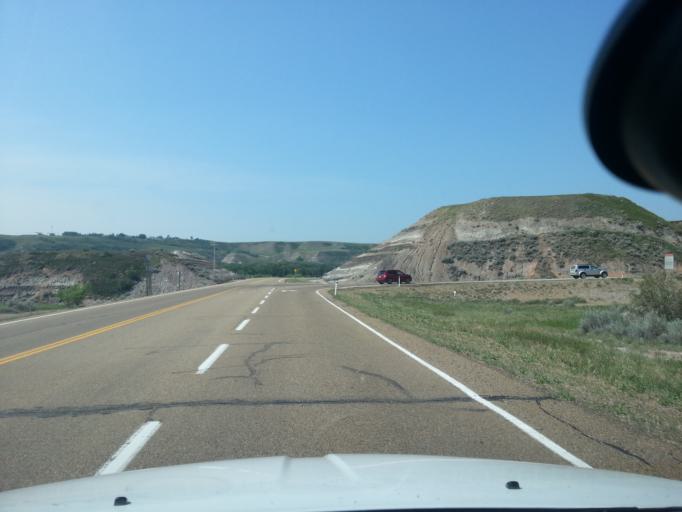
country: CA
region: Alberta
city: Three Hills
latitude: 51.4742
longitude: -112.7821
